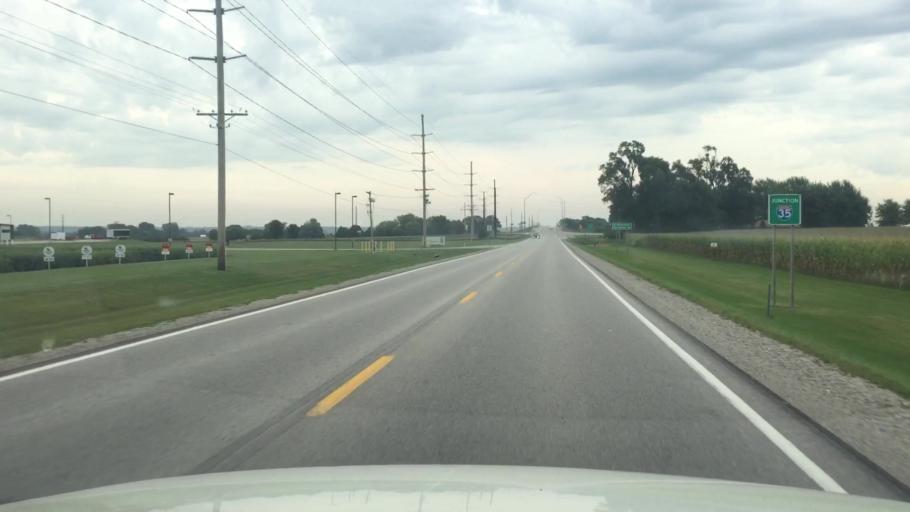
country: US
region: Iowa
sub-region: Story County
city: Huxley
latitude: 41.8778
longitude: -93.5778
